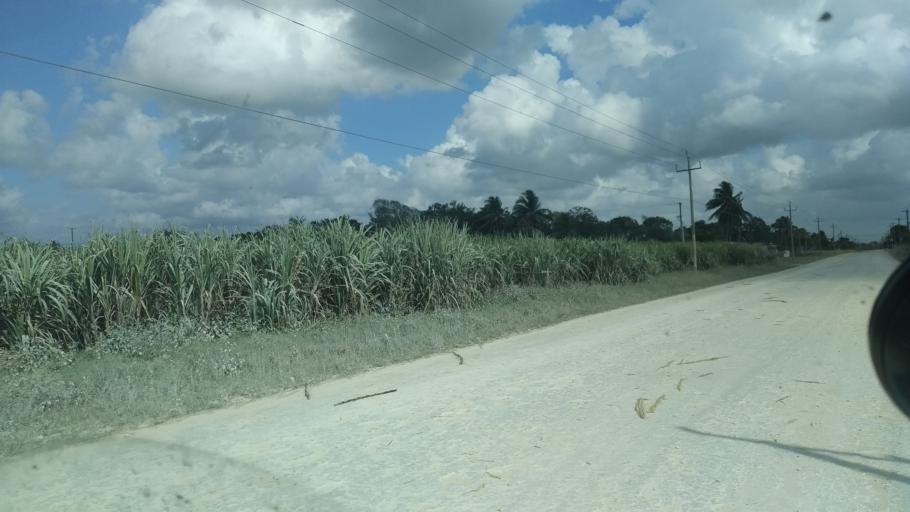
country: BZ
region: Corozal
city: Corozal
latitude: 18.3437
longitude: -88.4970
